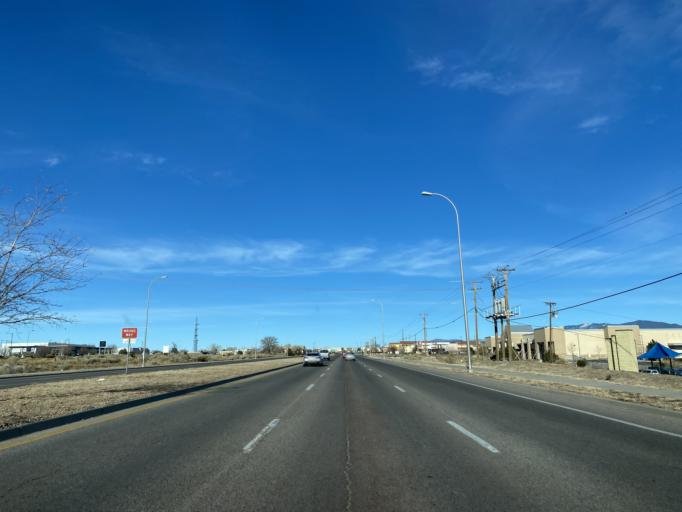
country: US
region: New Mexico
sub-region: Santa Fe County
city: Agua Fria
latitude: 35.6308
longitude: -106.0223
